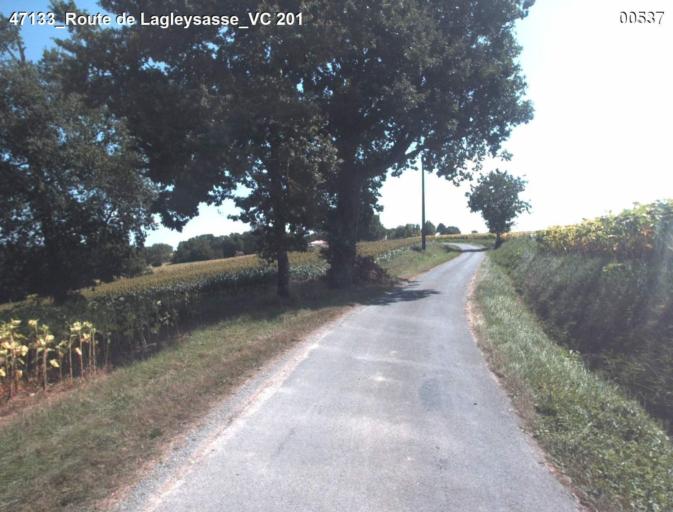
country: FR
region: Aquitaine
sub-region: Departement du Lot-et-Garonne
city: Laplume
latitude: 44.0600
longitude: 0.5534
